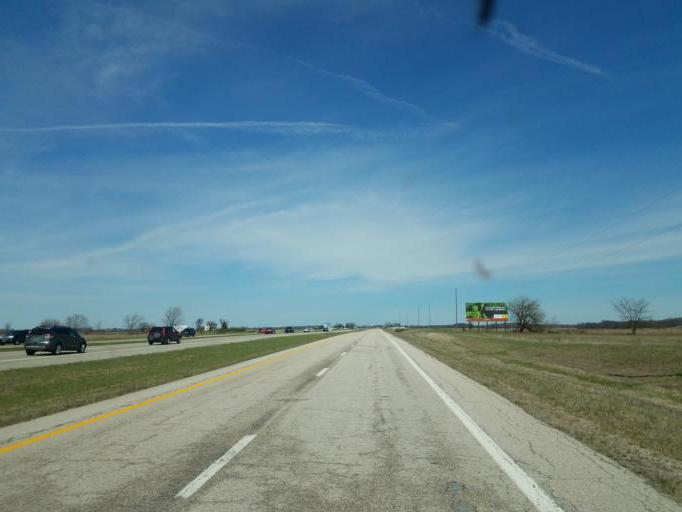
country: US
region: Ohio
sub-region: Delaware County
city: Delaware
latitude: 40.3976
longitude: -83.0737
